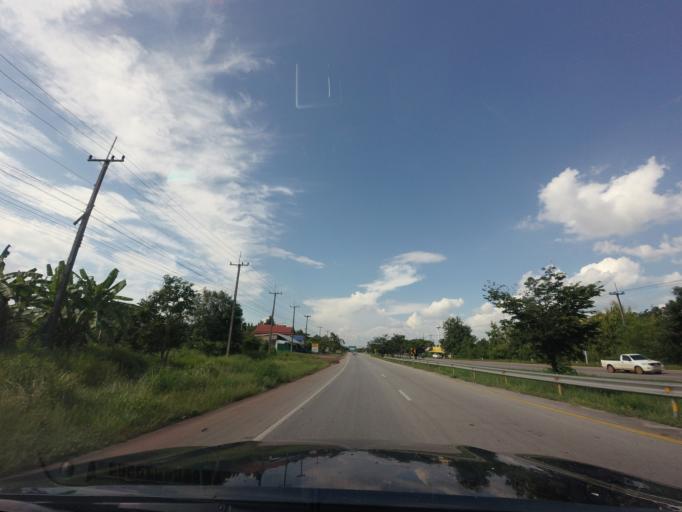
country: TH
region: Nong Khai
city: Sa Khrai
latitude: 17.6598
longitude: 102.7906
